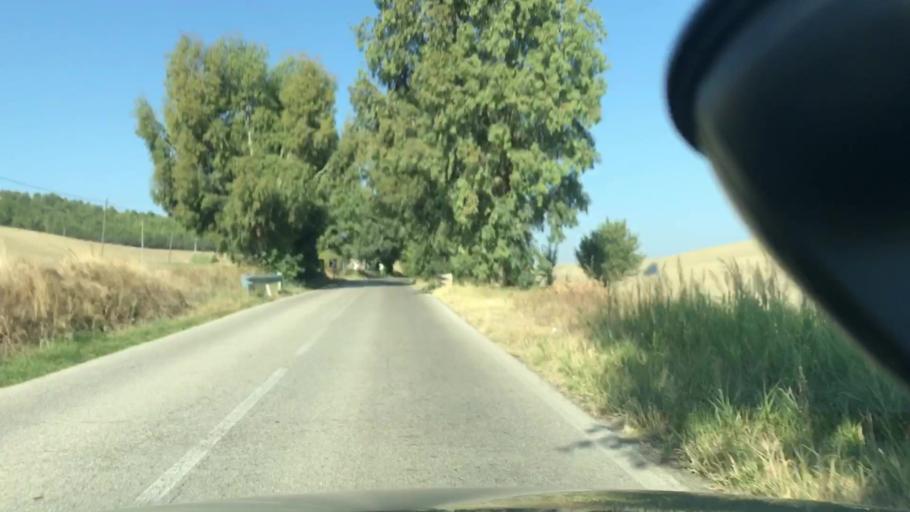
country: IT
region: Basilicate
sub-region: Provincia di Matera
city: La Martella
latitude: 40.6638
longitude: 16.4998
